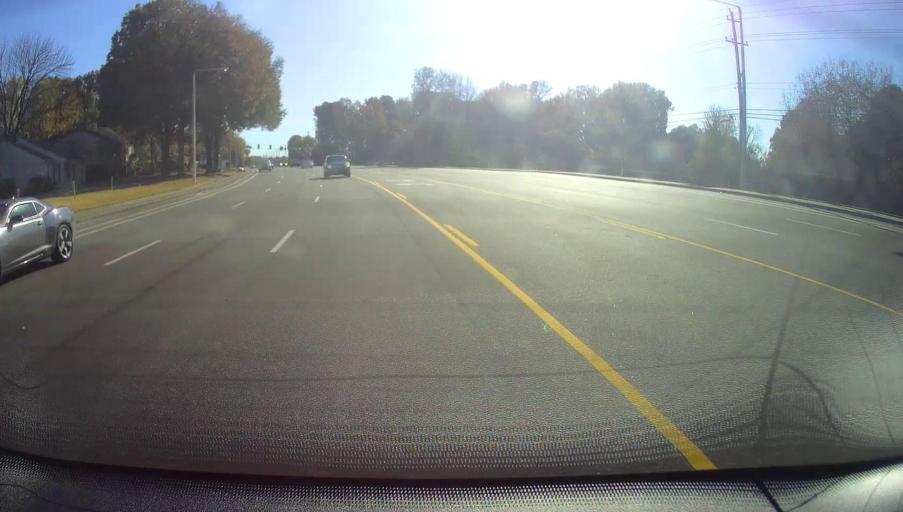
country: US
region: Tennessee
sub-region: Shelby County
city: Germantown
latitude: 35.0786
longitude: -89.8419
